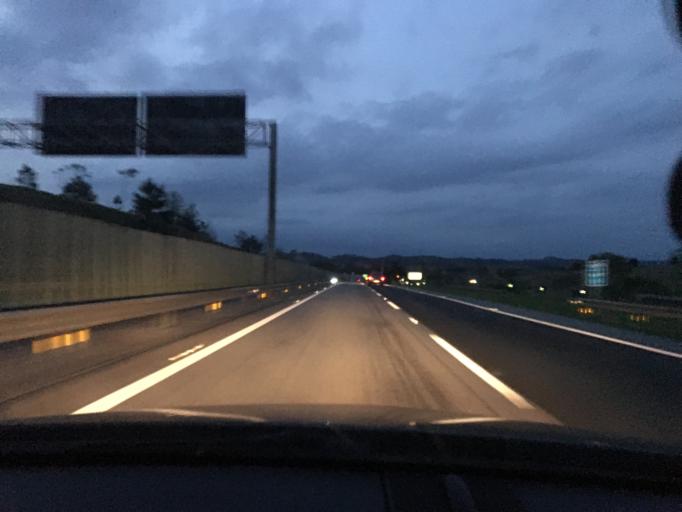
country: BR
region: Sao Paulo
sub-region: Santa Isabel
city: Santa Isabel
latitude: -23.3481
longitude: -46.1267
